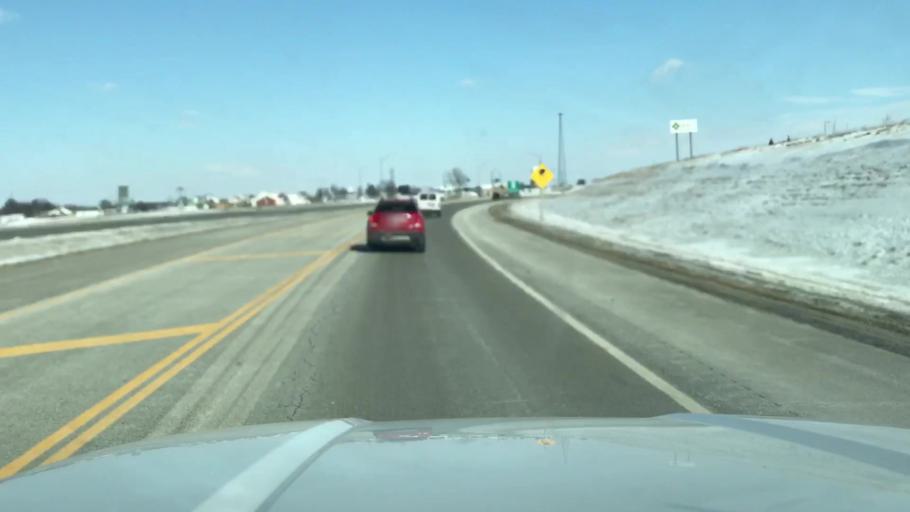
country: US
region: Missouri
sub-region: Nodaway County
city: Maryville
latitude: 40.3115
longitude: -94.8740
